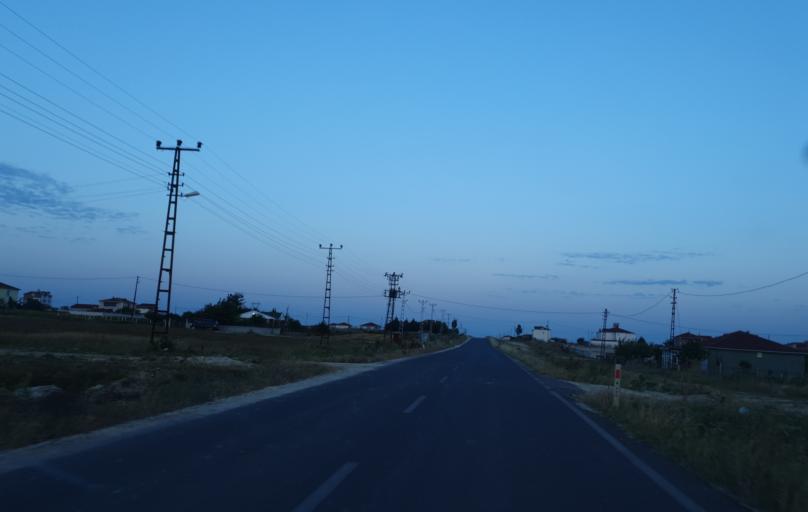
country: TR
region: Tekirdag
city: Velimese
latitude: 41.3438
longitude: 27.8968
